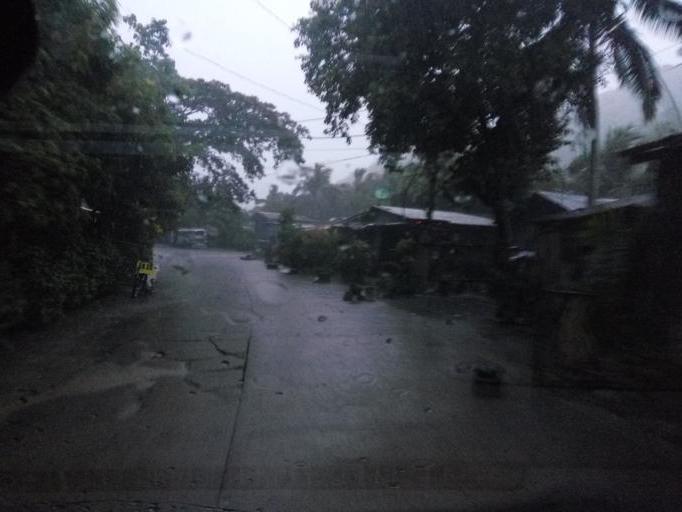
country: PH
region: Cagayan Valley
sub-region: Province of Nueva Vizcaya
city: Santa Fe
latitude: 16.1963
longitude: 120.9495
